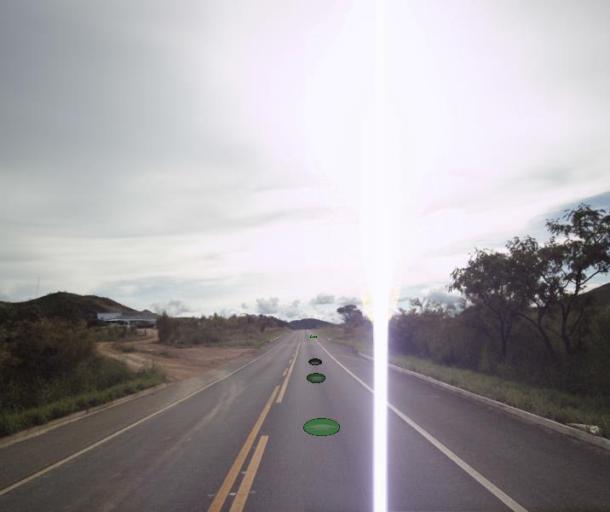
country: BR
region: Goias
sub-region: Barro Alto
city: Barro Alto
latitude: -15.1218
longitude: -48.7159
